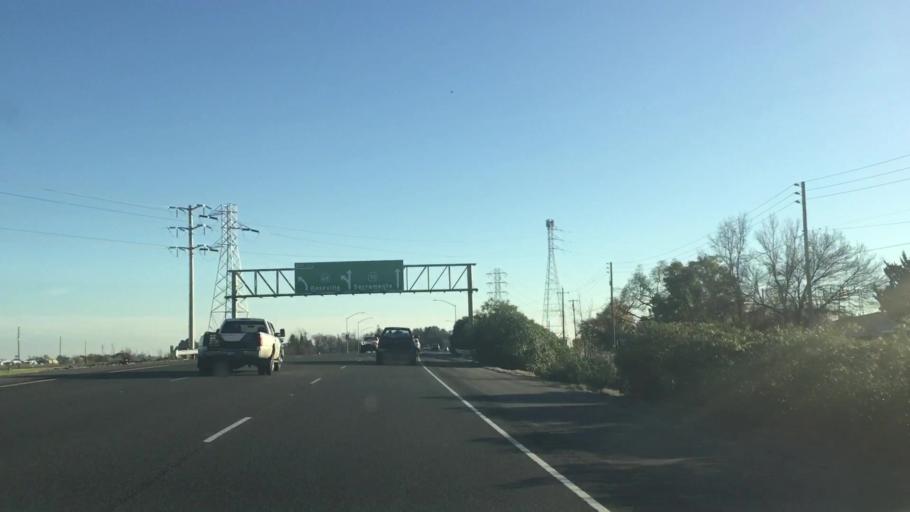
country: US
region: California
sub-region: Yuba County
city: Olivehurst
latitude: 39.0949
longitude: -121.5429
